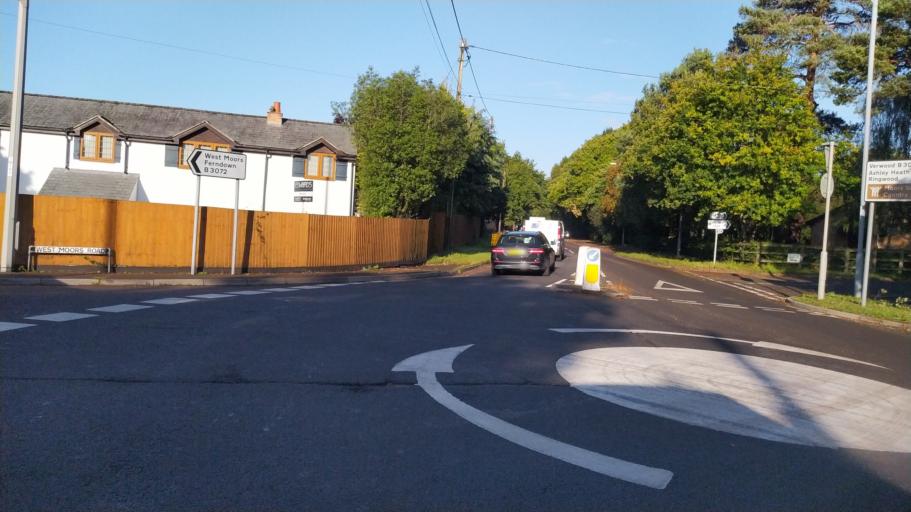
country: GB
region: England
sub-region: Dorset
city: Three Legged Cross
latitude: 50.8506
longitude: -1.8879
